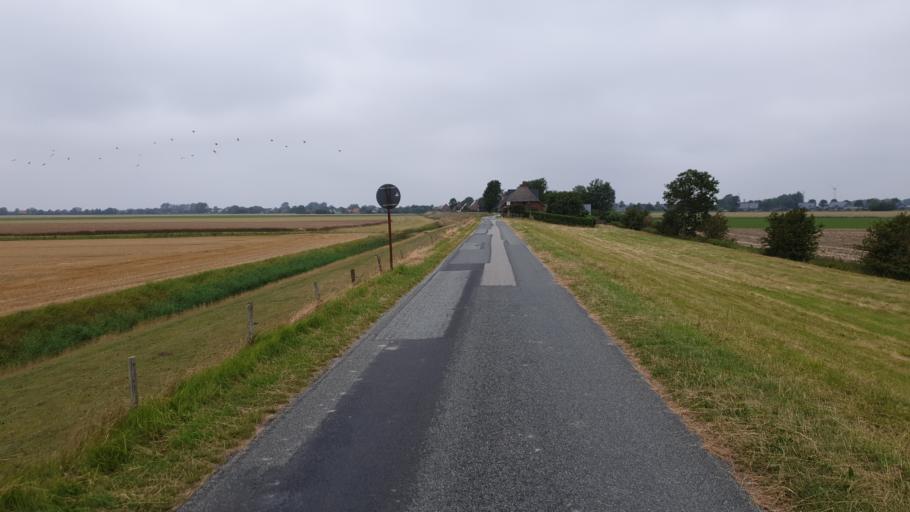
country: DE
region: Schleswig-Holstein
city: Elisabeth-Sophien-Koog
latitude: 54.4808
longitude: 8.8933
